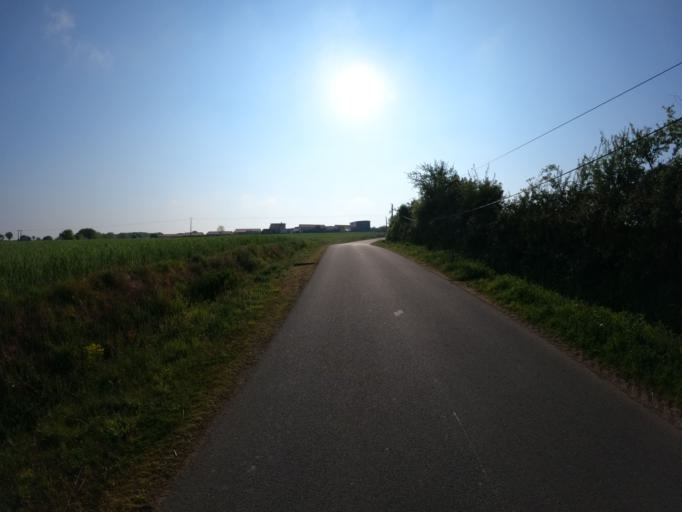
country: FR
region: Pays de la Loire
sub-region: Departement de Maine-et-Loire
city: La Seguiniere
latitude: 47.0675
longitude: -0.9561
